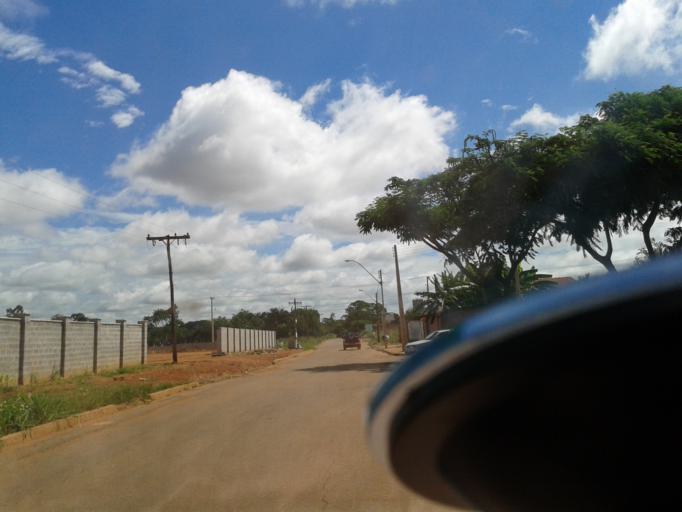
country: BR
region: Goias
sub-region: Goiania
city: Goiania
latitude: -16.6468
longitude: -49.3463
